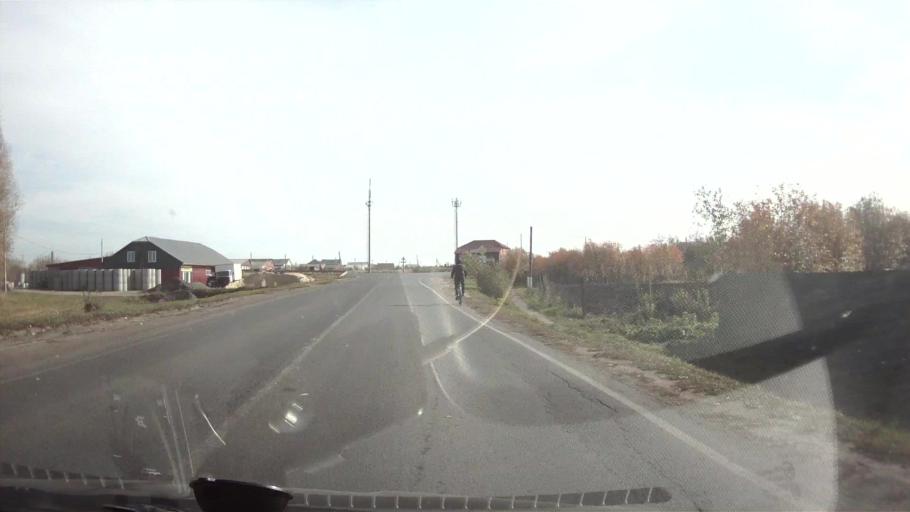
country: RU
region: Mordoviya
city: Turgenevo
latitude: 54.8439
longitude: 46.3504
